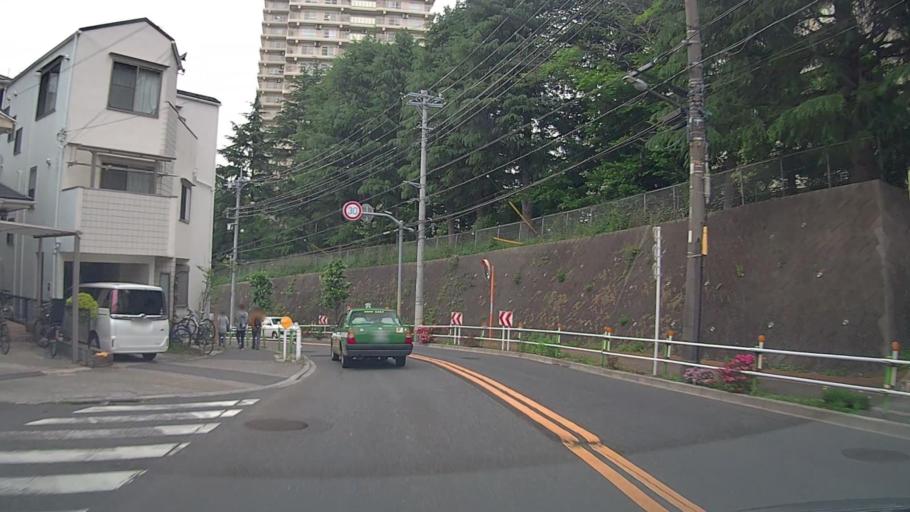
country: JP
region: Saitama
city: Shimotoda
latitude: 35.7742
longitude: 139.6777
